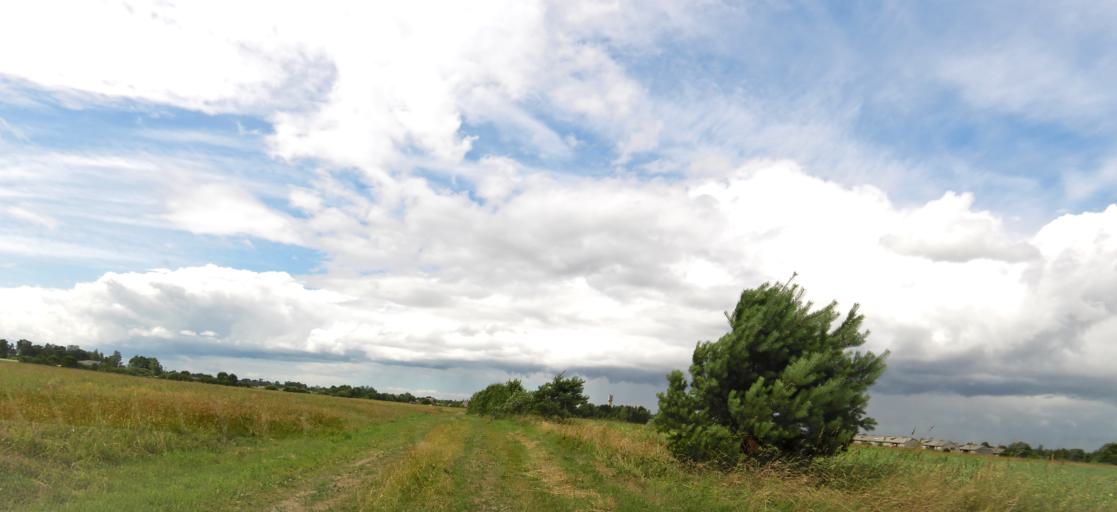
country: LT
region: Panevezys
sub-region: Birzai
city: Birzai
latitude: 56.3942
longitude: 24.7866
